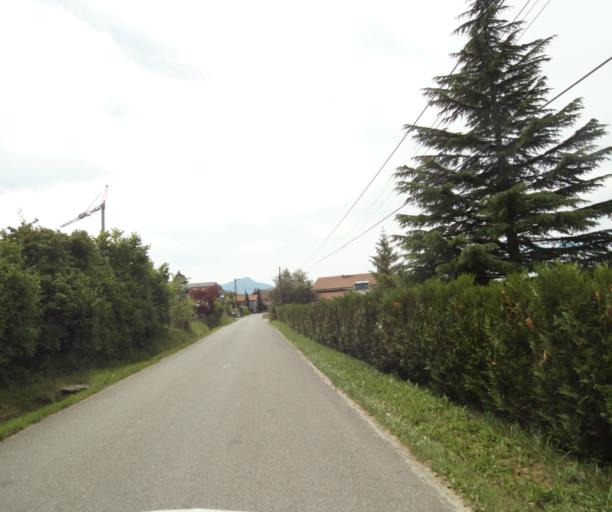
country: FR
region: Rhone-Alpes
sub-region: Departement de la Haute-Savoie
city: Anthy-sur-Leman
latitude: 46.3494
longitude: 6.4118
